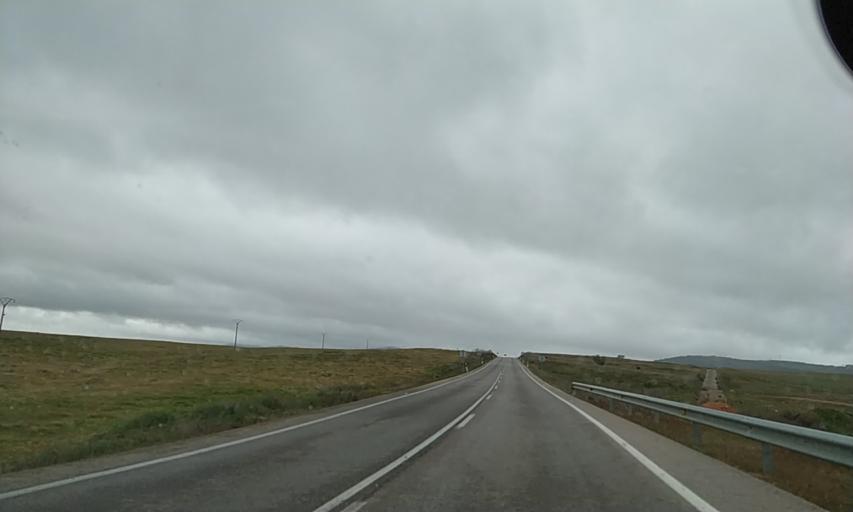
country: ES
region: Extremadura
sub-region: Provincia de Caceres
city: Caceres
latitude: 39.5176
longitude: -6.3976
